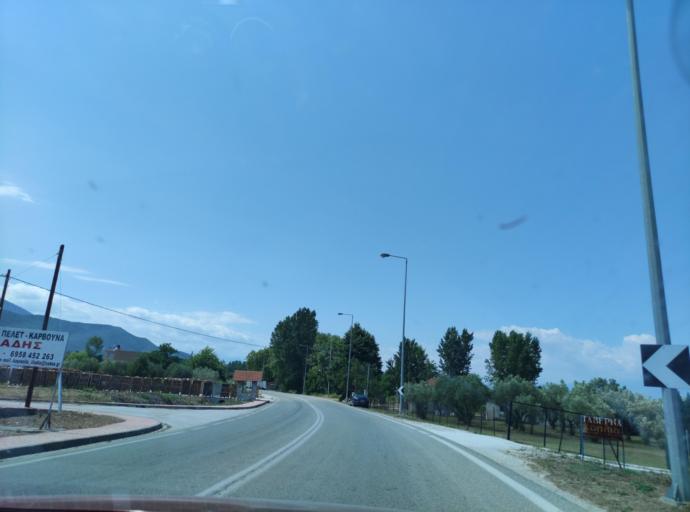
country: GR
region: East Macedonia and Thrace
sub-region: Nomos Kavalas
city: Palaiochori
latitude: 40.9495
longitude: 24.2079
